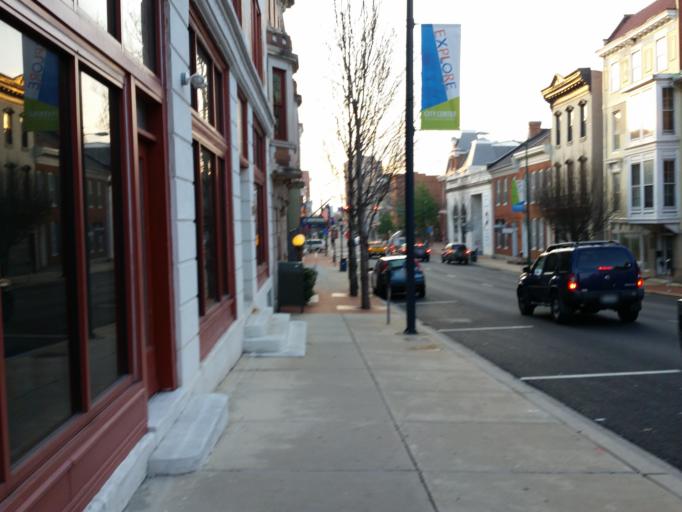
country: US
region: Maryland
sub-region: Washington County
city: Hagerstown
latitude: 39.6436
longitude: -77.7238
